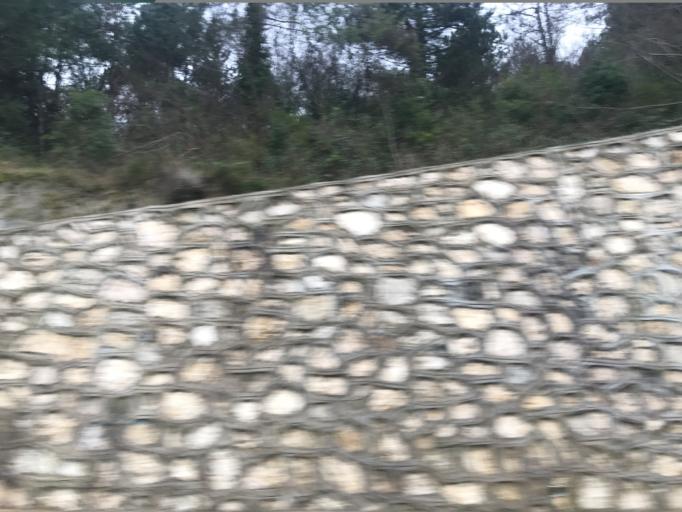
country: TR
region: Bartin
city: Amasra
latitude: 41.7338
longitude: 32.3726
